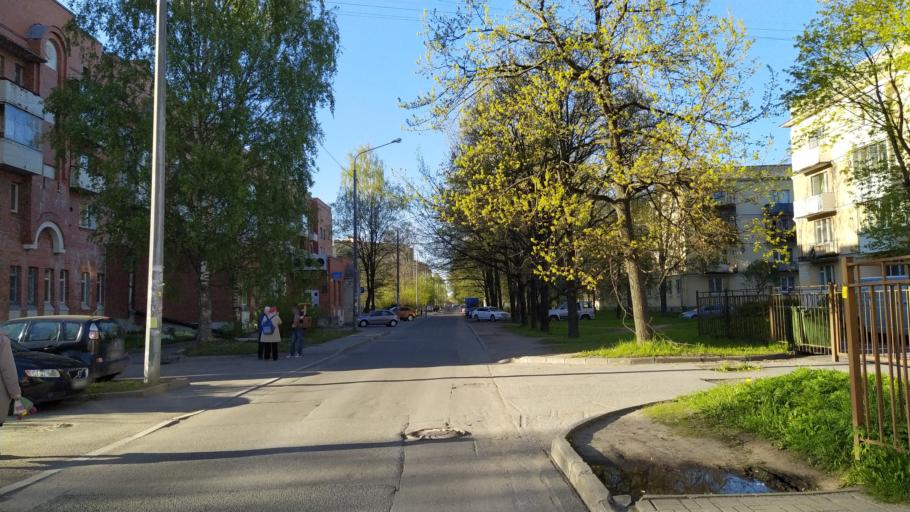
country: RU
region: St.-Petersburg
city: Pavlovsk
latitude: 59.6866
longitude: 30.4284
